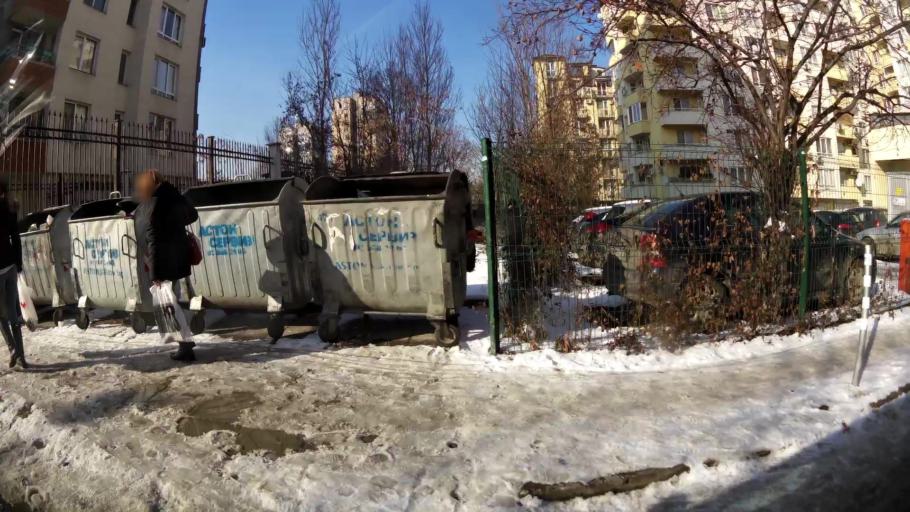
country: BG
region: Sofia-Capital
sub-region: Stolichna Obshtina
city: Sofia
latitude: 42.6633
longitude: 23.3462
